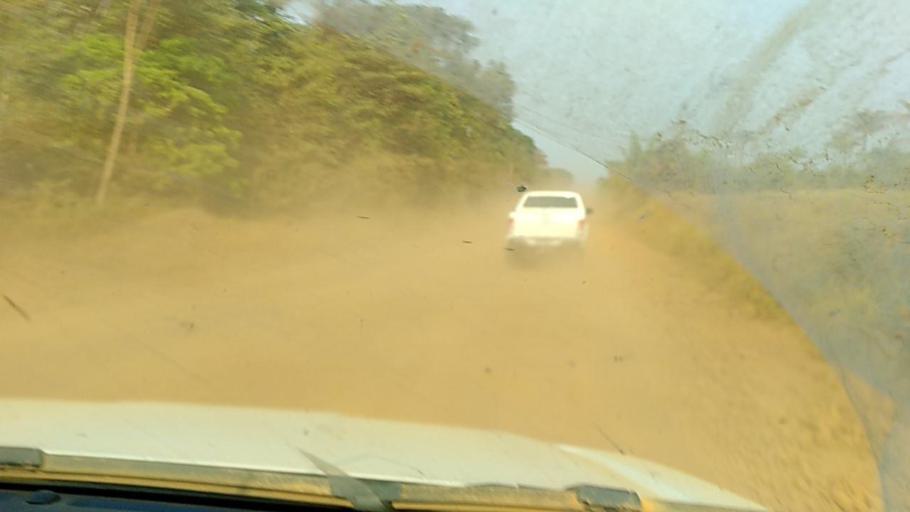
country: BR
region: Rondonia
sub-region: Porto Velho
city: Porto Velho
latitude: -8.7589
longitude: -63.9615
